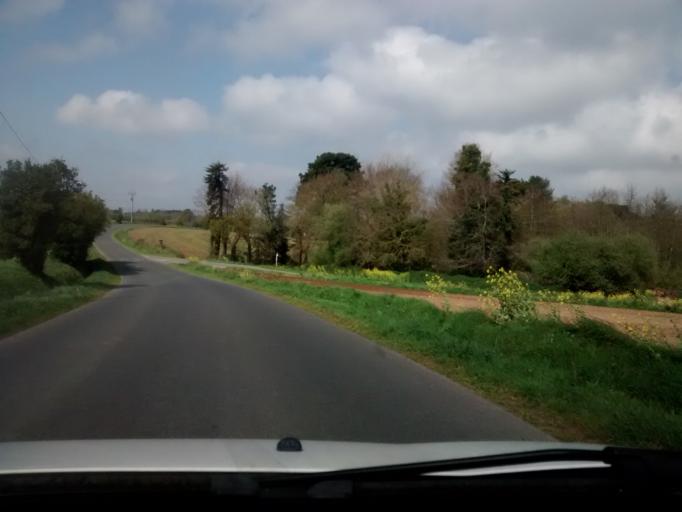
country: FR
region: Brittany
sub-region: Departement des Cotes-d'Armor
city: Trevou-Treguignec
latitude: 48.7893
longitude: -3.3371
